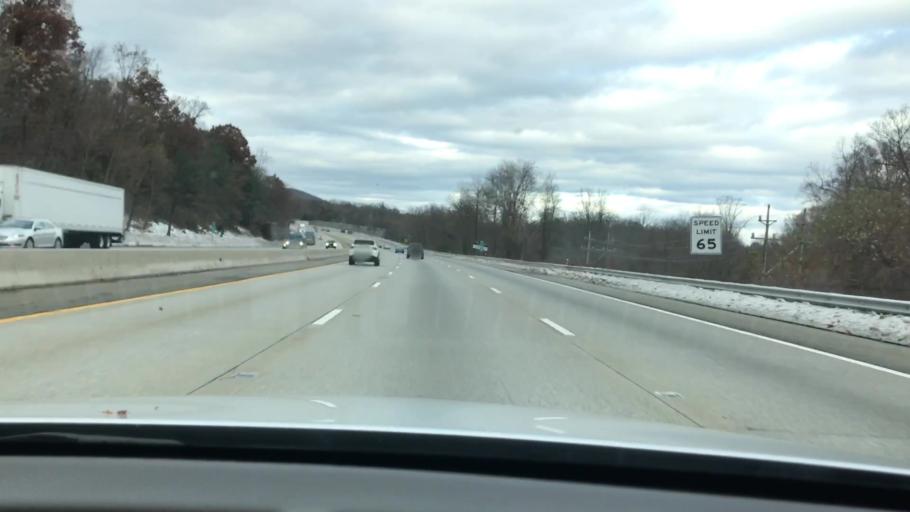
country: US
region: New Jersey
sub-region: Morris County
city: Boonton
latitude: 40.9221
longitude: -74.3620
